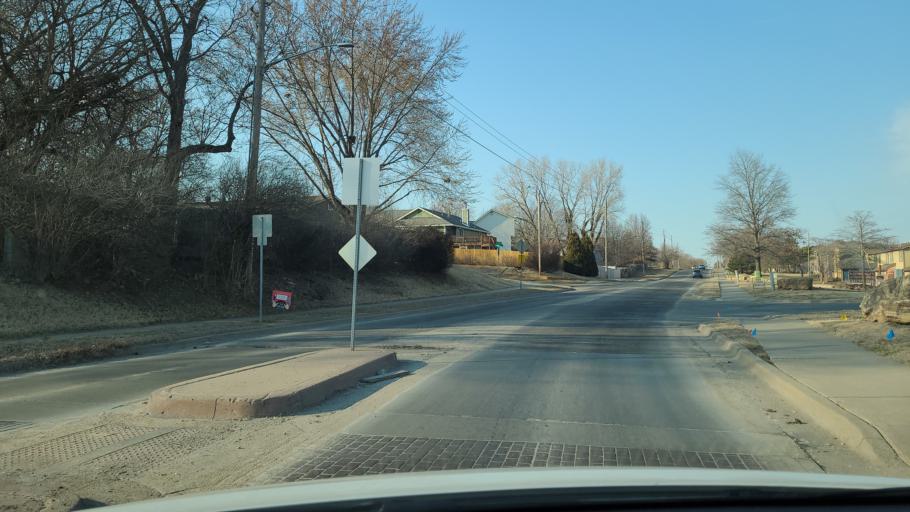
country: US
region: Kansas
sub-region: Douglas County
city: Lawrence
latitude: 38.9641
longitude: -95.2883
